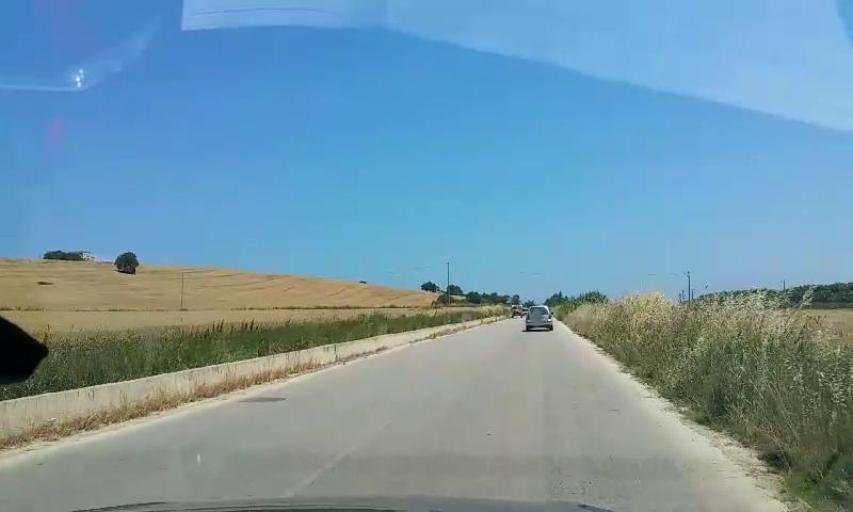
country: IT
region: Molise
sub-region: Provincia di Campobasso
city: Termoli
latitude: 41.9994
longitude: 14.9559
